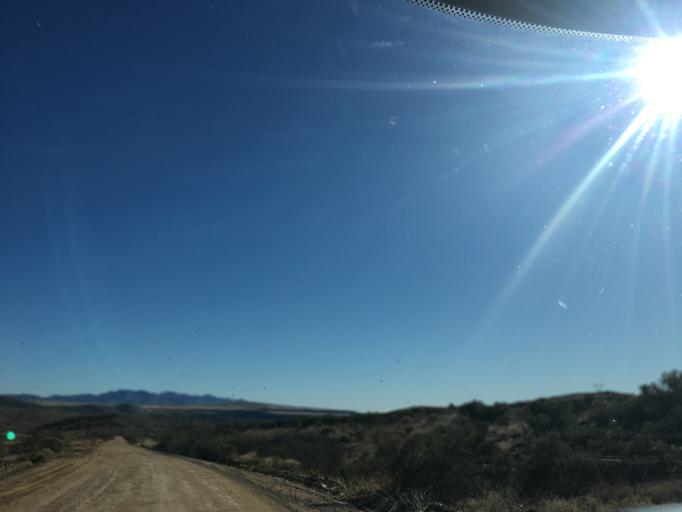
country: US
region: Arizona
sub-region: Yavapai County
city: Cordes Lakes
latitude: 34.2785
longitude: -112.1157
